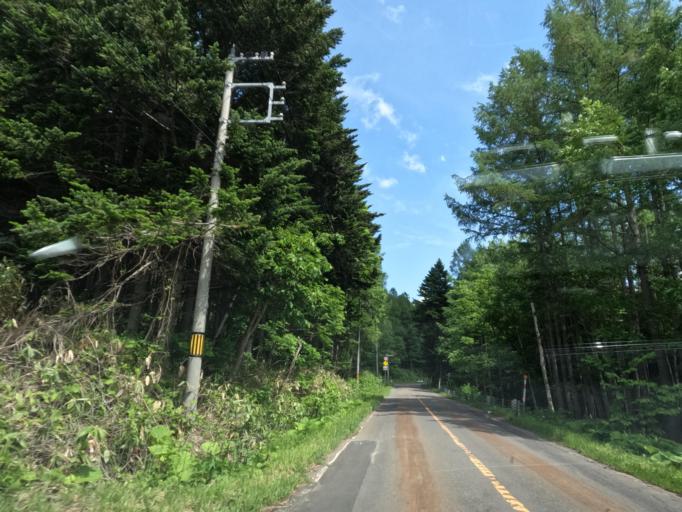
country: JP
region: Hokkaido
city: Takikawa
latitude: 43.5784
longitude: 141.8322
